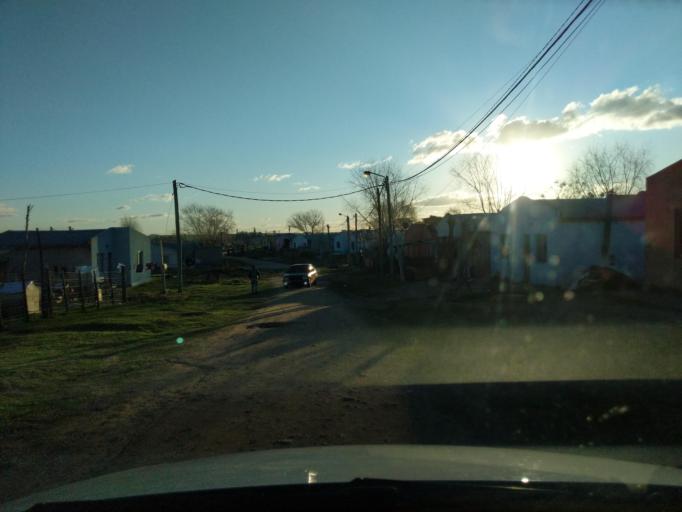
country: UY
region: Florida
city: Florida
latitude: -34.1031
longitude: -56.2360
